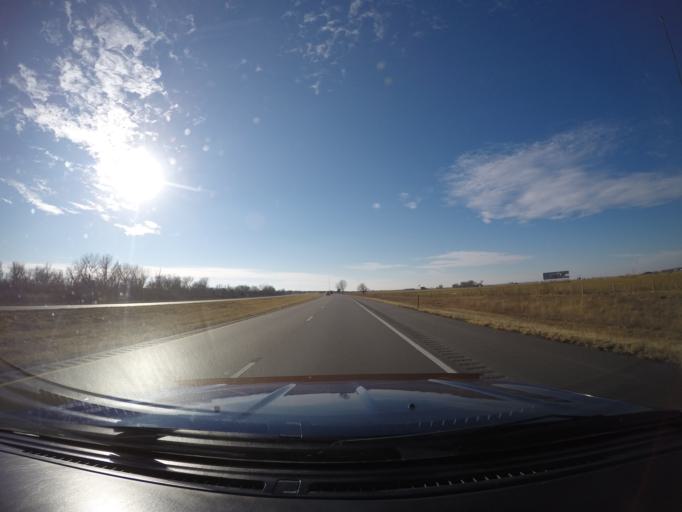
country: US
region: Nebraska
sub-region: Buffalo County
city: Gibbon
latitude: 40.6902
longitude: -98.9402
